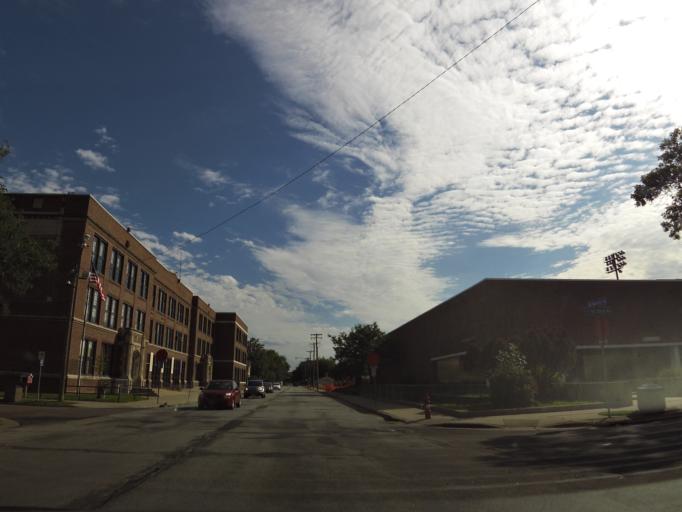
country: US
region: Minnesota
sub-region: Hennepin County
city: Minneapolis
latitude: 45.0102
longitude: -93.2526
